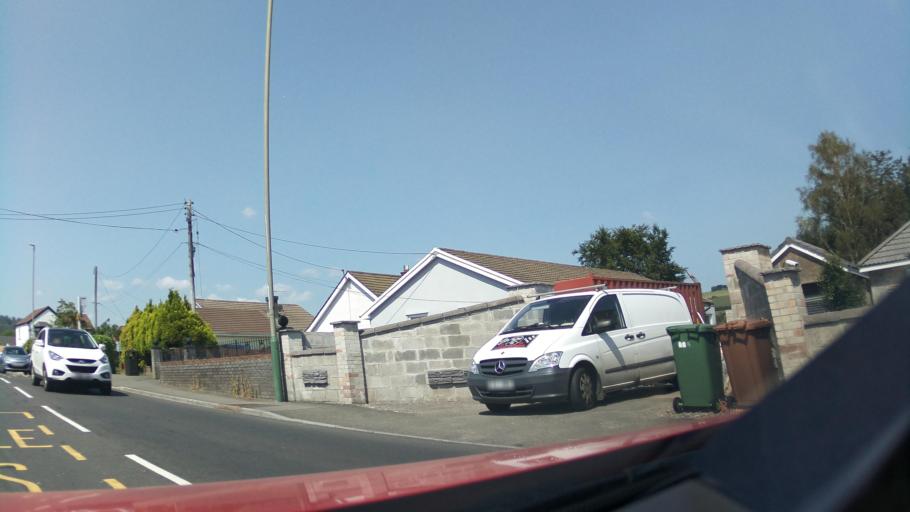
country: GB
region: Wales
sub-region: Caerphilly County Borough
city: Caerphilly
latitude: 51.5893
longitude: -3.2231
